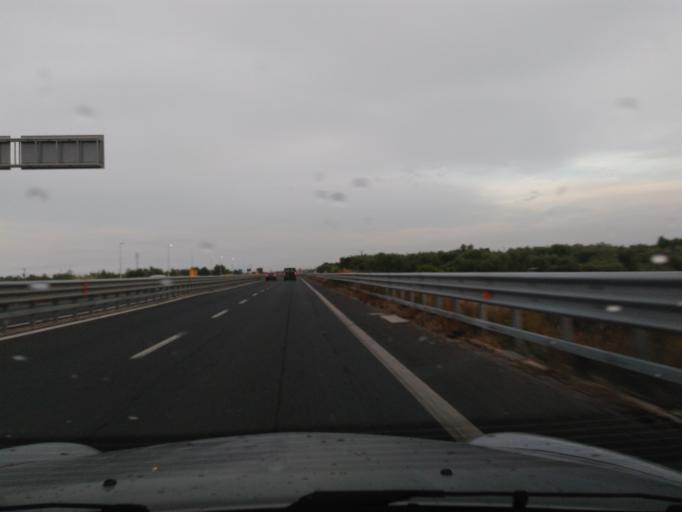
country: IT
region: Apulia
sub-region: Provincia di Bari
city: Giovinazzo
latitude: 41.1738
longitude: 16.6770
